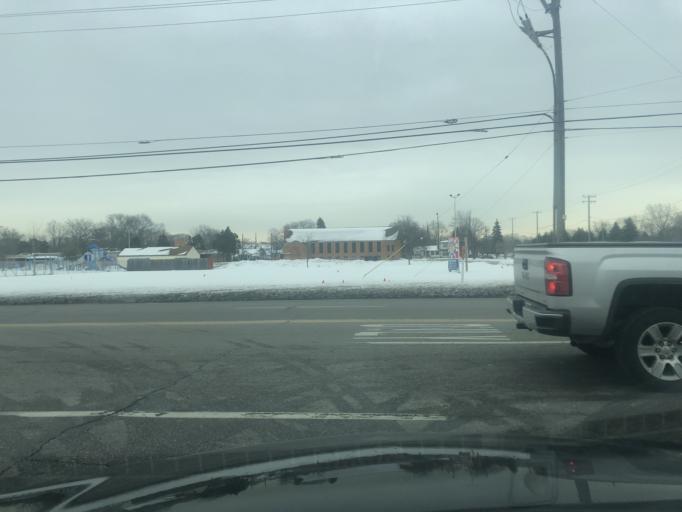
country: US
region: Michigan
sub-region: Wayne County
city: Redford
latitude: 42.4145
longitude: -83.2966
